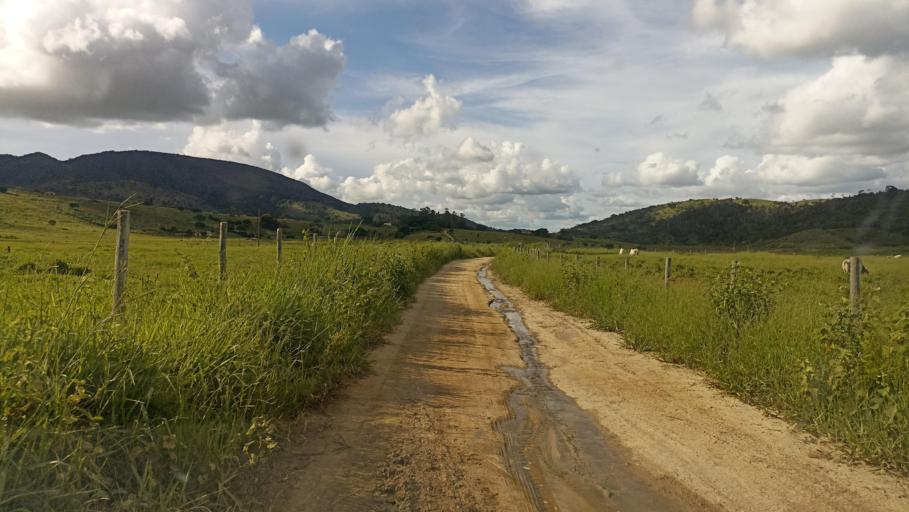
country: BR
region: Minas Gerais
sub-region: Almenara
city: Almenara
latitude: -16.6198
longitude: -40.4646
